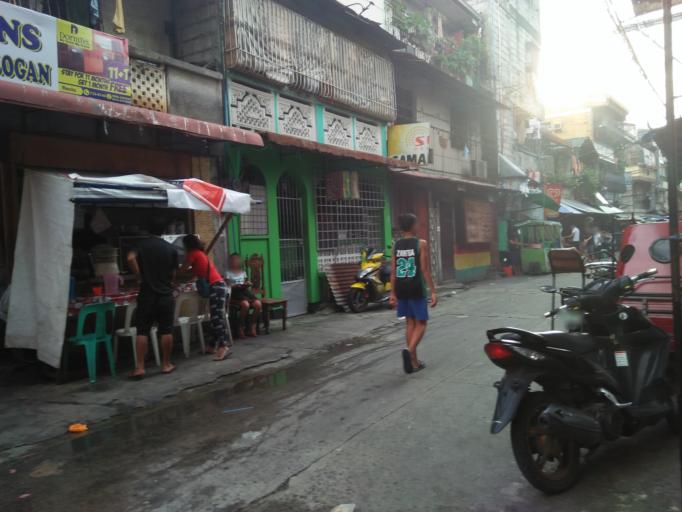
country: PH
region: Metro Manila
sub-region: San Juan
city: San Juan
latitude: 14.5997
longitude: 121.0210
